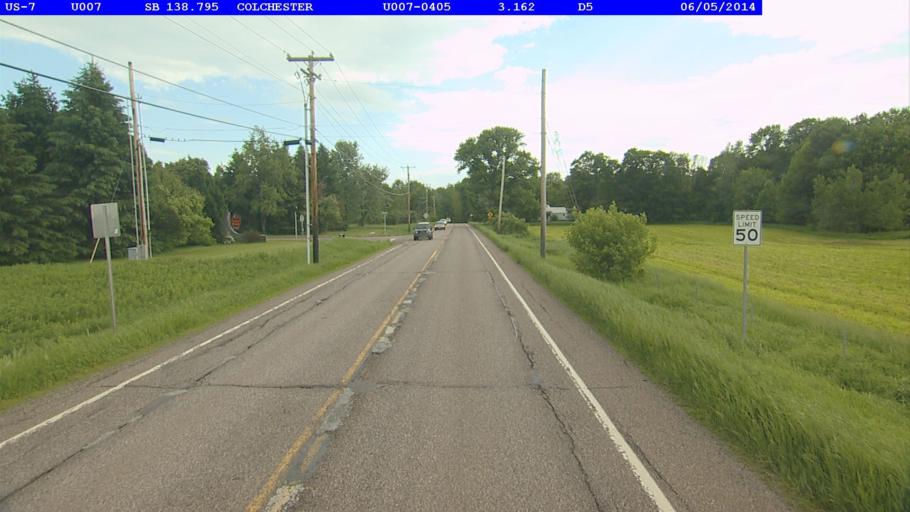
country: US
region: Vermont
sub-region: Chittenden County
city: Colchester
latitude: 44.5446
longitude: -73.1671
